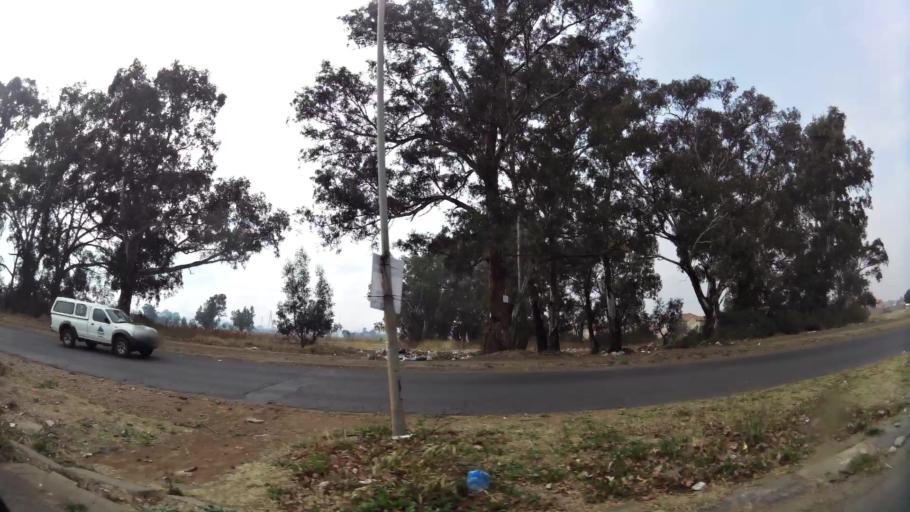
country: ZA
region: Gauteng
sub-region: Sedibeng District Municipality
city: Vanderbijlpark
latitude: -26.6779
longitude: 27.8381
